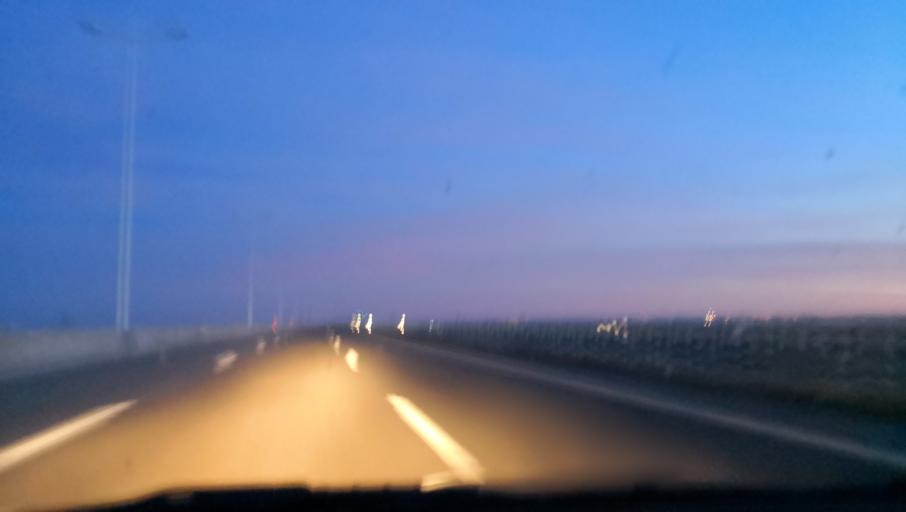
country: PT
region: Lisbon
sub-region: Vila Franca de Xira
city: Castanheira do Ribatejo
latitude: 39.0006
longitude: -8.9053
